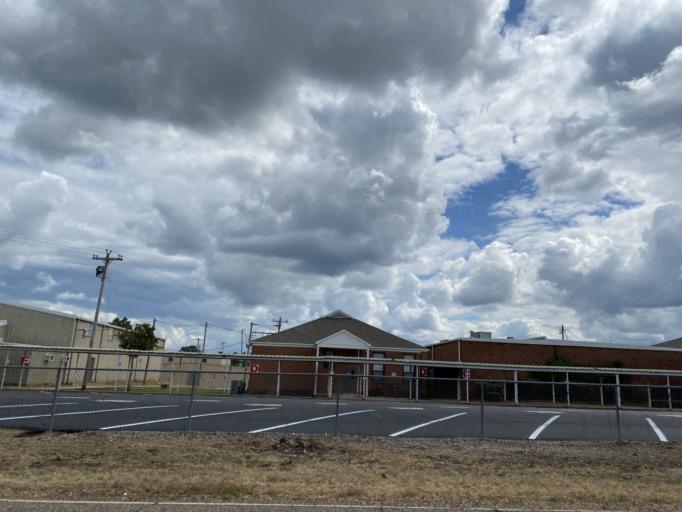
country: US
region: Mississippi
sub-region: Monroe County
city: Amory
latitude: 33.9770
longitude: -88.4154
